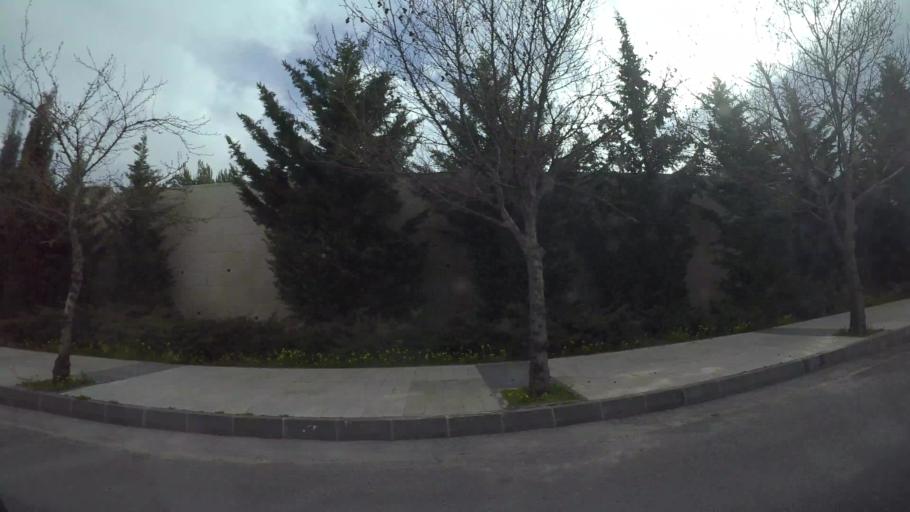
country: JO
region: Amman
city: Wadi as Sir
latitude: 31.9825
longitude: 35.8215
